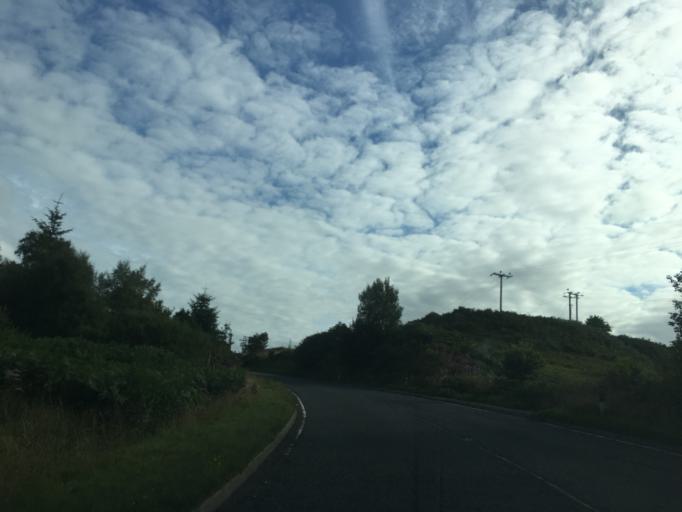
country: GB
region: Scotland
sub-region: Argyll and Bute
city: Oban
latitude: 56.3958
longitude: -5.4697
